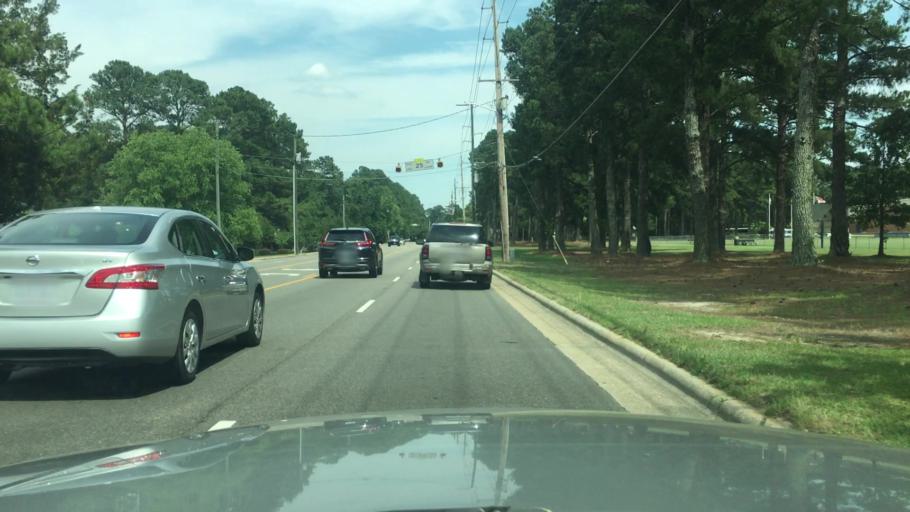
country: US
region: North Carolina
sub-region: Cumberland County
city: Fayetteville
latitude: 35.0655
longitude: -78.9427
